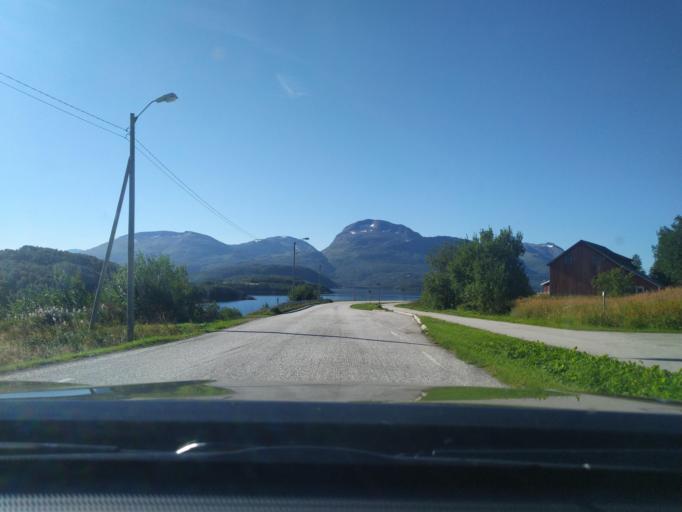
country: NO
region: Troms
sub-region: Salangen
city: Sjovegan
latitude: 68.9360
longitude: 17.7164
